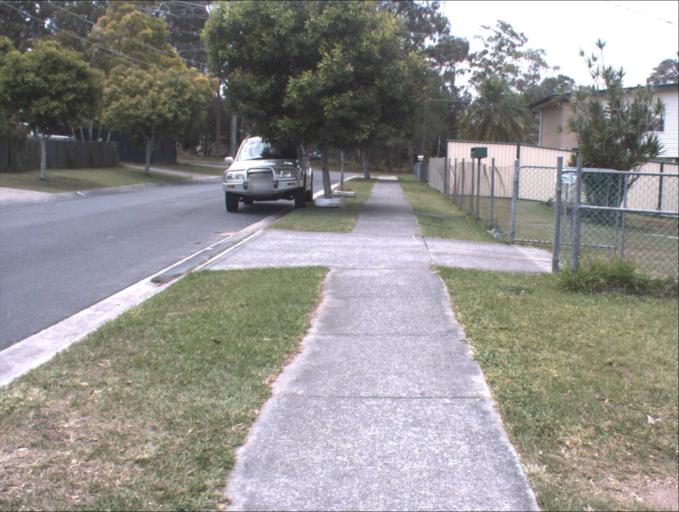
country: AU
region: Queensland
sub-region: Logan
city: Woodridge
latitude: -27.6376
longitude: 153.0976
